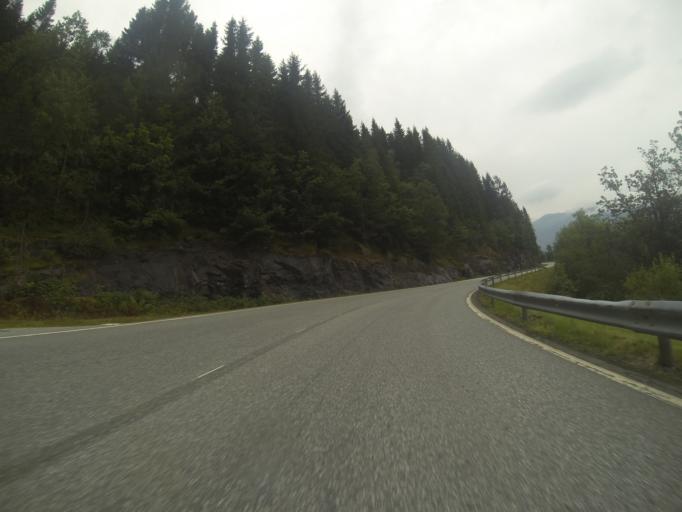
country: NO
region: Rogaland
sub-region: Suldal
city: Sand
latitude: 59.5573
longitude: 6.2607
